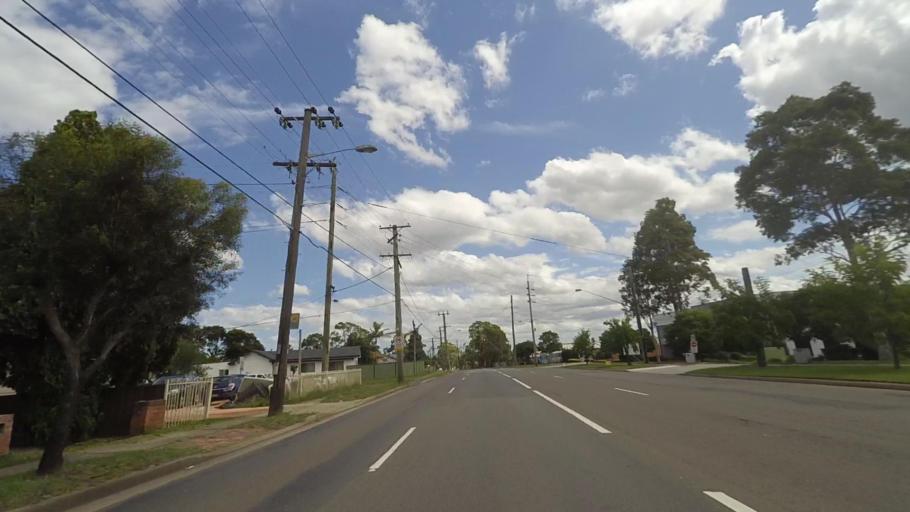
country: AU
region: New South Wales
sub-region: Holroyd
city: Guildford West
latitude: -33.8516
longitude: 150.9606
